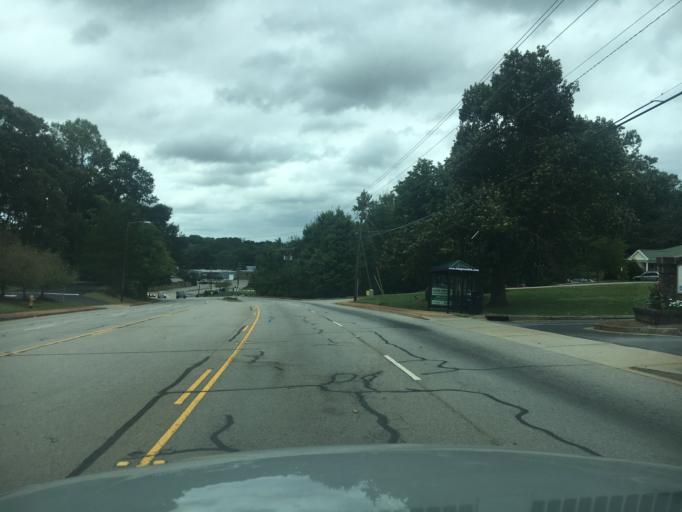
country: US
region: South Carolina
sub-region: Greenville County
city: Greenville
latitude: 34.8774
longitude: -82.3930
